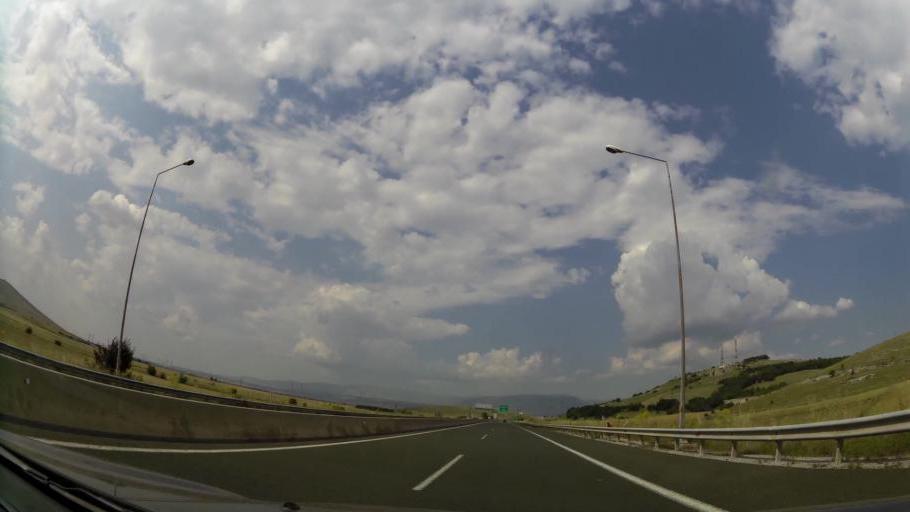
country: GR
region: West Macedonia
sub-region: Nomos Kozanis
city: Koila
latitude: 40.3530
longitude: 21.8110
